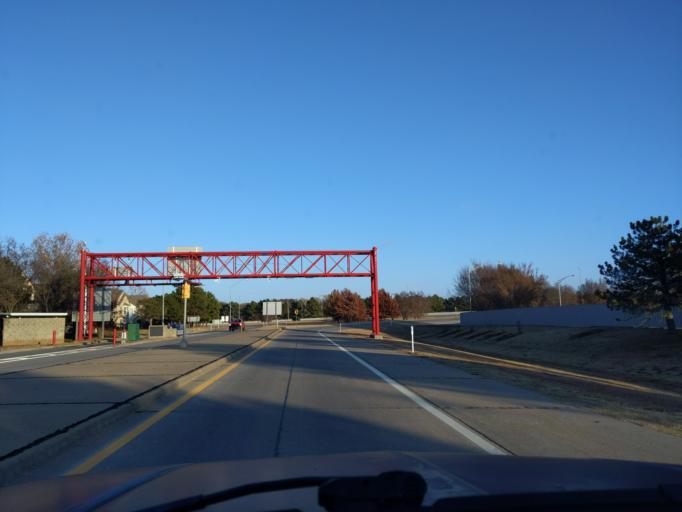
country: US
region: Oklahoma
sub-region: Tulsa County
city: Jenks
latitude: 36.0217
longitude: -95.9479
